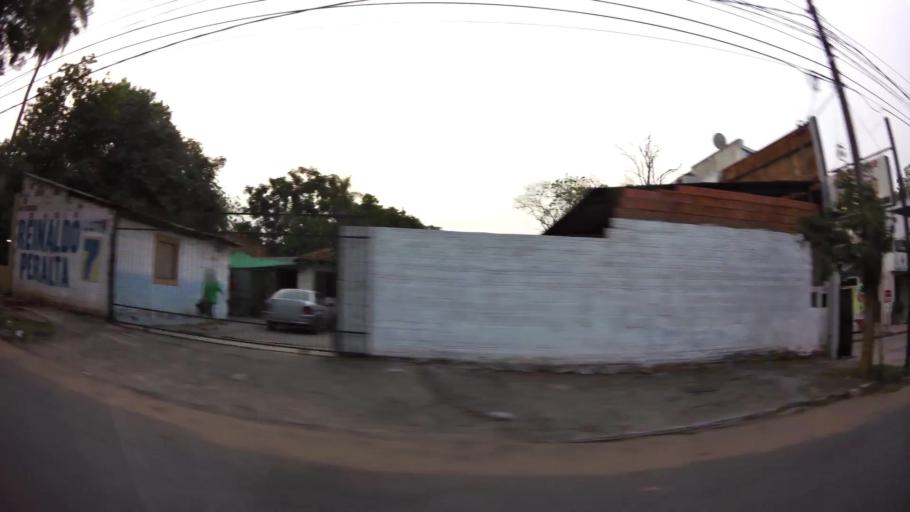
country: PY
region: Central
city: Lambare
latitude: -25.3259
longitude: -57.6173
